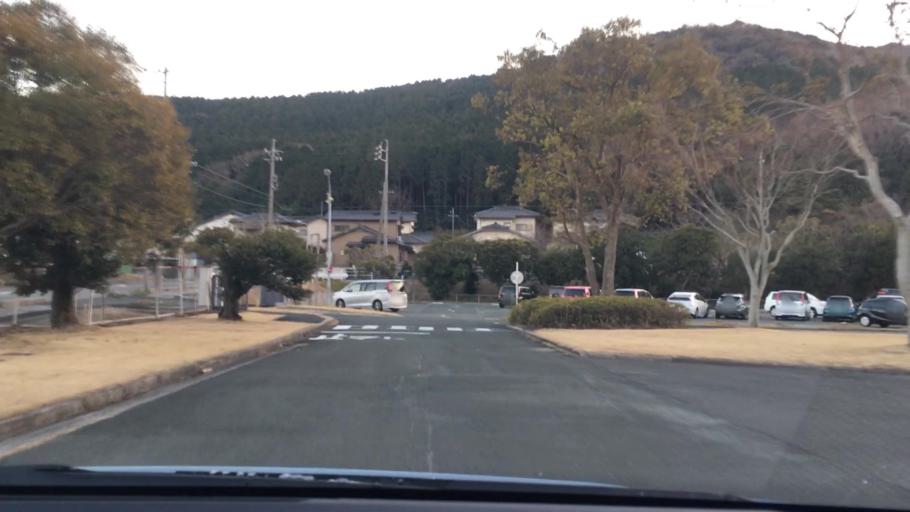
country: JP
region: Aichi
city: Tahara
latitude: 34.6698
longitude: 137.2478
